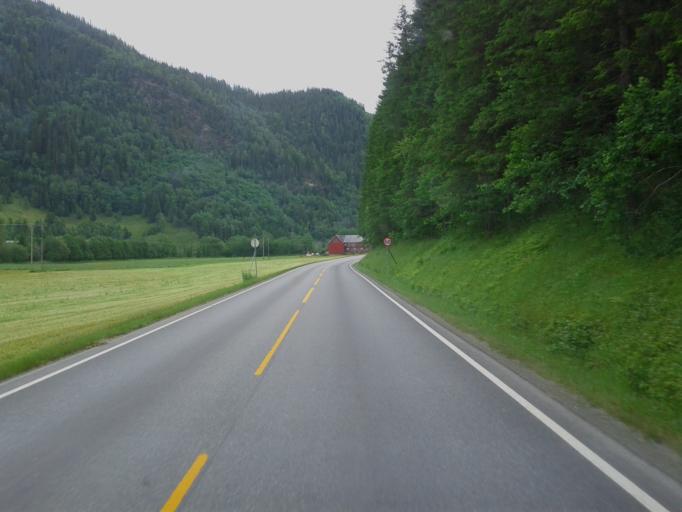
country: NO
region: Sor-Trondelag
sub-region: Midtre Gauldal
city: Storen
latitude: 62.9679
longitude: 10.5729
